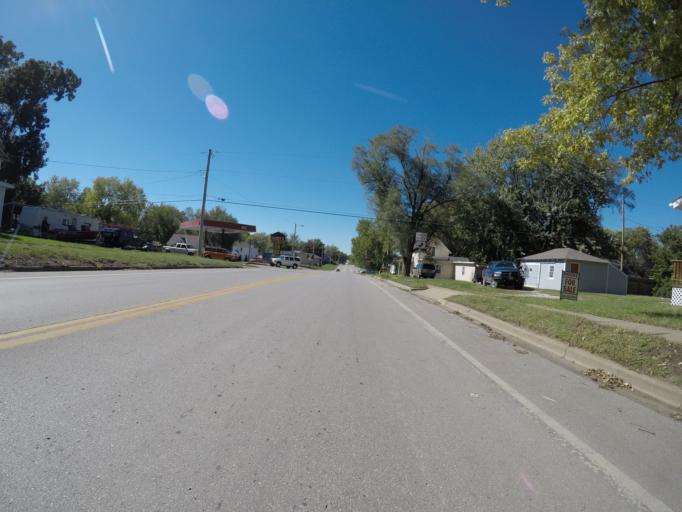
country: US
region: Kansas
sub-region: Douglas County
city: Eudora
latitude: 38.9420
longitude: -95.0951
